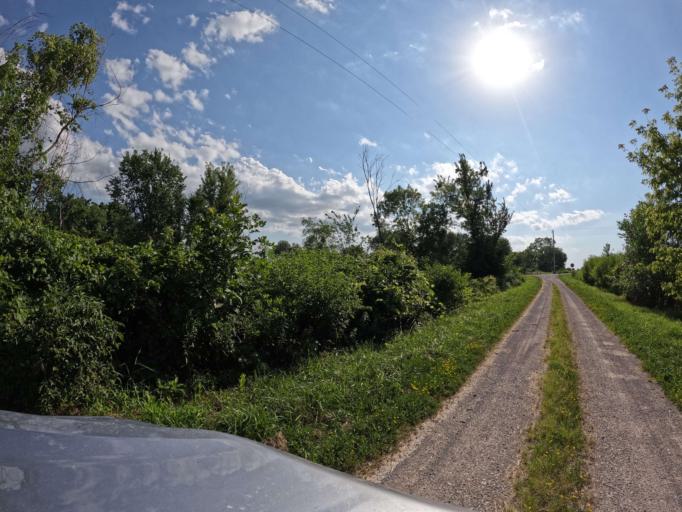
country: US
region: Iowa
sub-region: Appanoose County
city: Centerville
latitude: 40.7203
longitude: -93.0292
